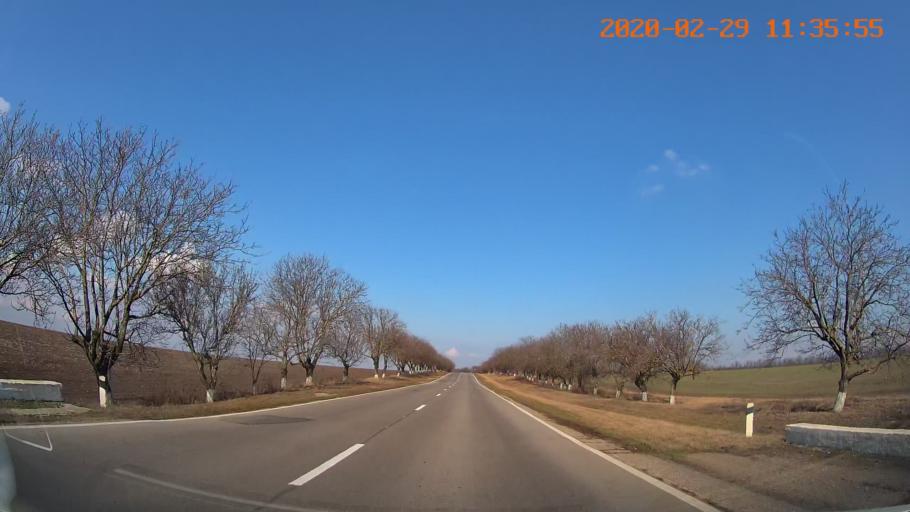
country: MD
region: Rezina
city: Saharna
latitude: 47.5878
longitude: 29.0601
